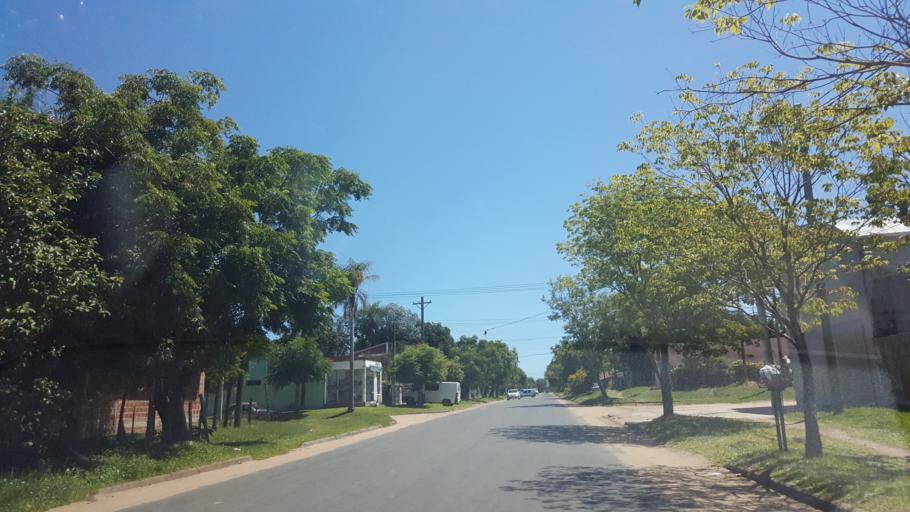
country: AR
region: Corrientes
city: Ituzaingo
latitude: -27.5929
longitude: -56.6935
